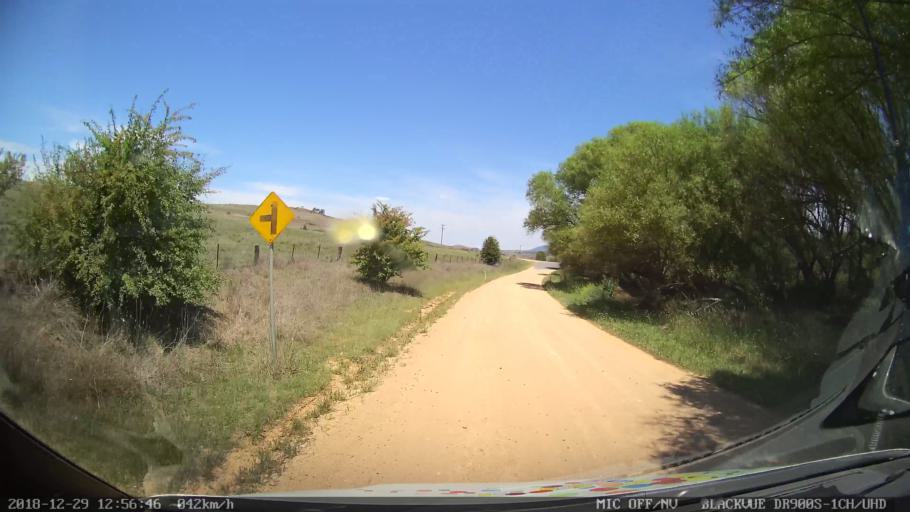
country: AU
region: Australian Capital Territory
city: Macarthur
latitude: -35.7035
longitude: 149.1807
